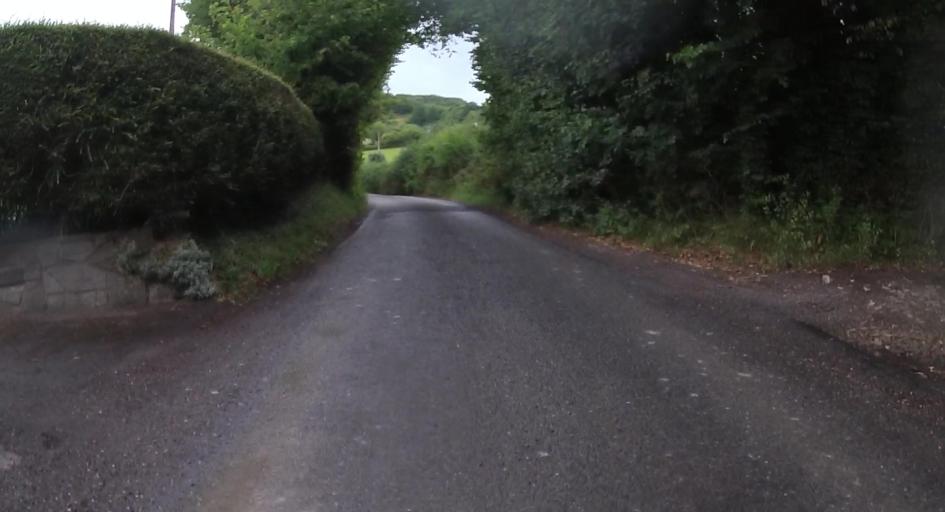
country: GB
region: England
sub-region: Hampshire
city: Long Sutton
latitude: 51.1938
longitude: -0.9146
